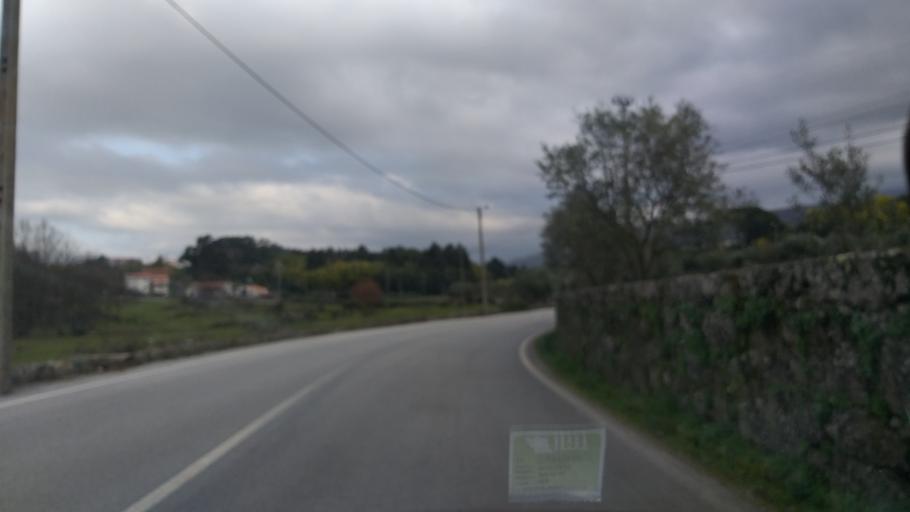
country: PT
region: Guarda
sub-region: Manteigas
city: Manteigas
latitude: 40.5008
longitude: -7.6168
